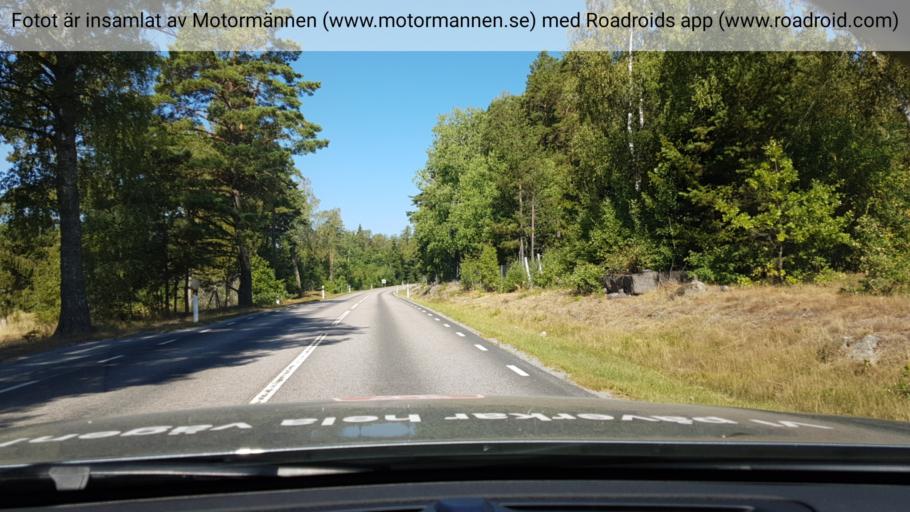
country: SE
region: Stockholm
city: Stenhamra
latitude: 59.3048
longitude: 17.6473
